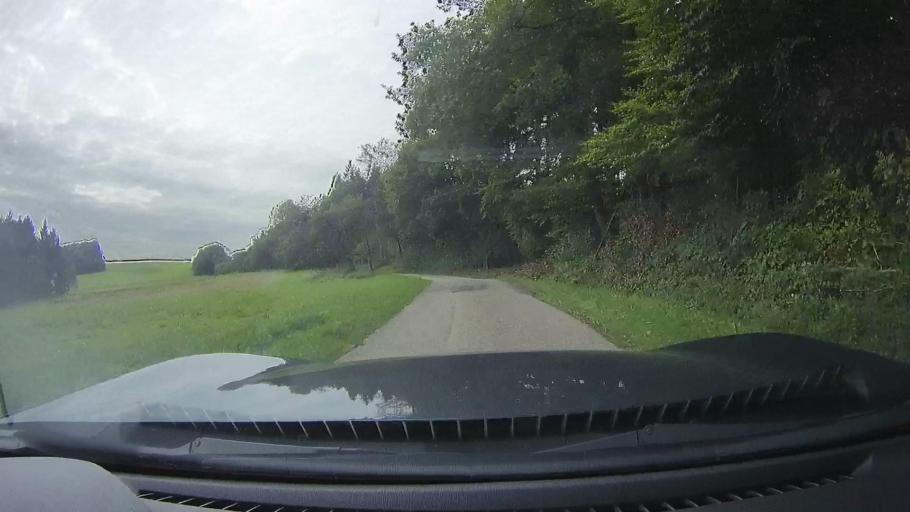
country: DE
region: Baden-Wuerttemberg
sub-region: Regierungsbezirk Stuttgart
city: Wustenrot
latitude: 49.0568
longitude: 9.4720
